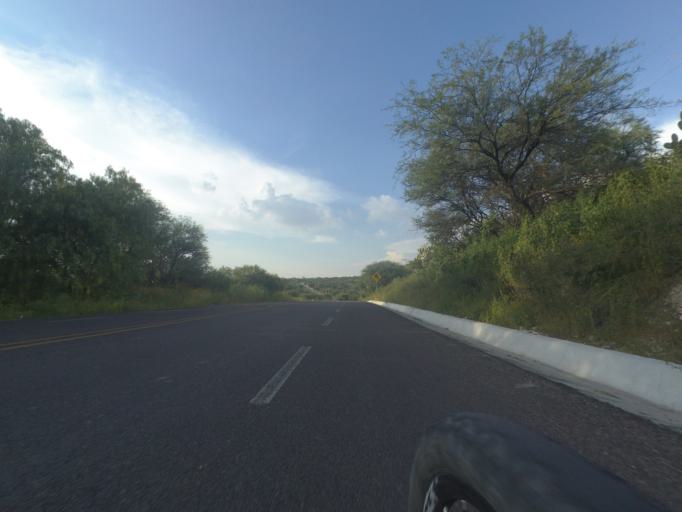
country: MX
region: Aguascalientes
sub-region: Aguascalientes
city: Penuelas (El Cienegal)
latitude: 21.7578
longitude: -102.3504
